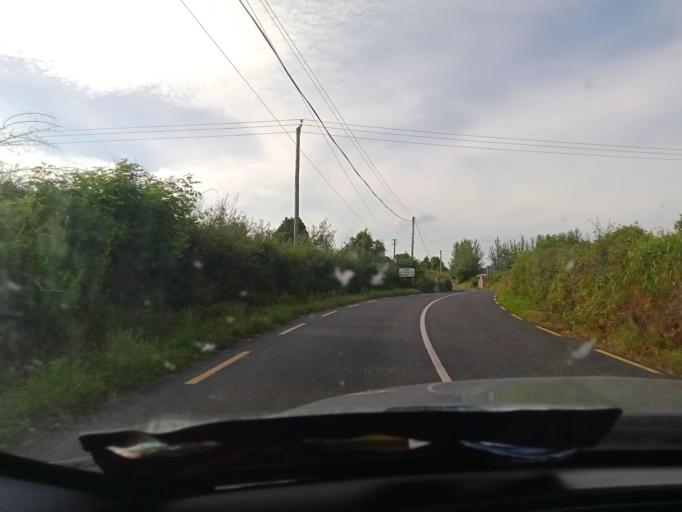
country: IE
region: Leinster
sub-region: An Longfort
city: Granard
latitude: 53.7960
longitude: -7.4031
